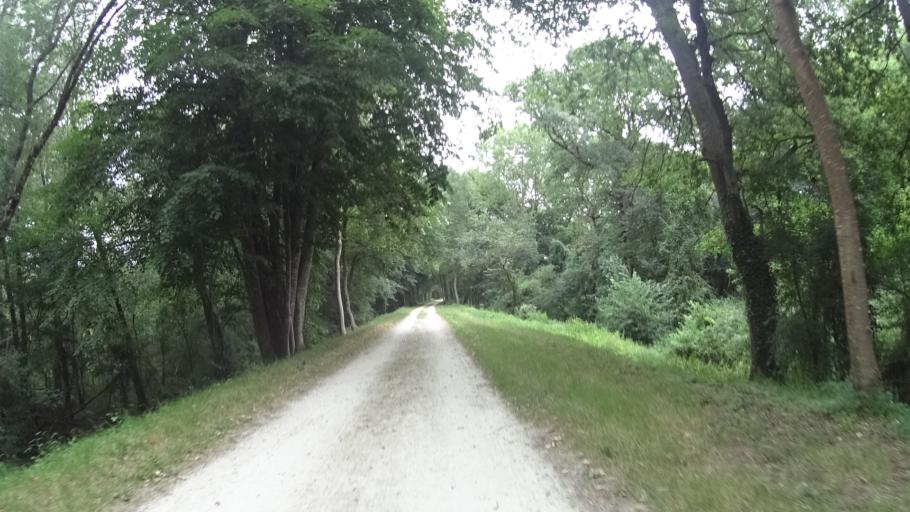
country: FR
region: Centre
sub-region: Departement d'Indre-et-Loire
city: Huismes
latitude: 47.2511
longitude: 0.2502
